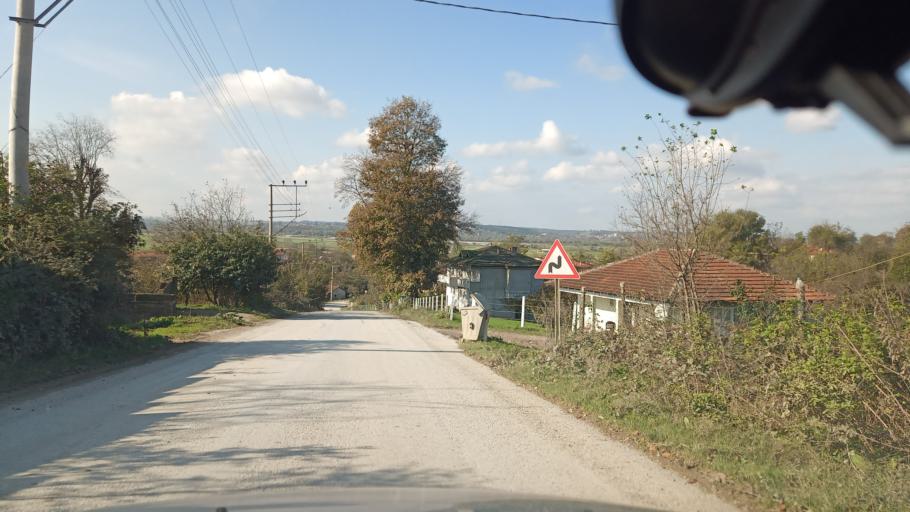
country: TR
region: Sakarya
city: Kaynarca
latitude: 41.0913
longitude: 30.4488
